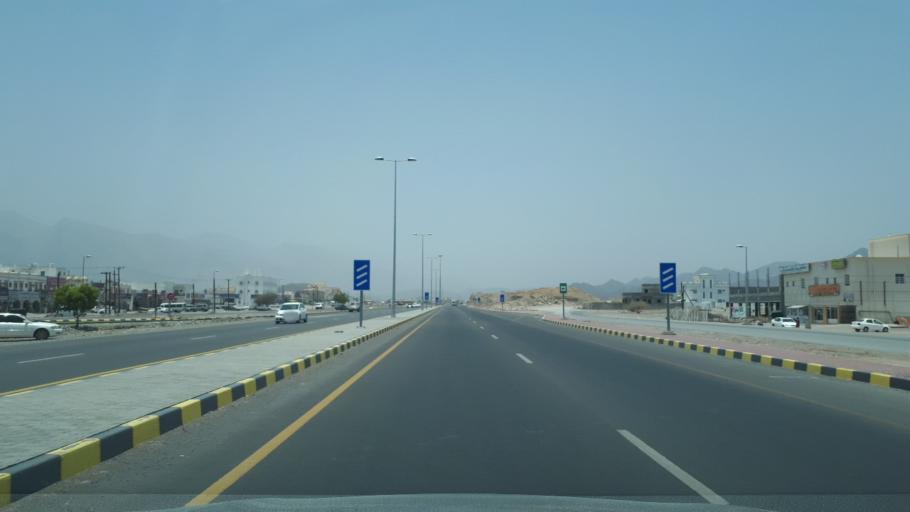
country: OM
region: Al Batinah
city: Rustaq
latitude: 23.4360
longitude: 57.3927
